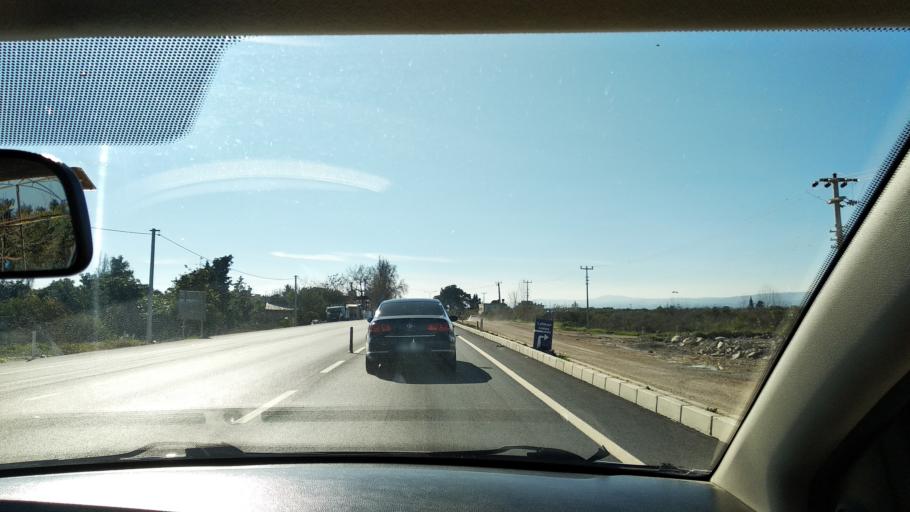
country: TR
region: Mersin
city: Tomuk
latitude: 36.6683
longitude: 34.4029
